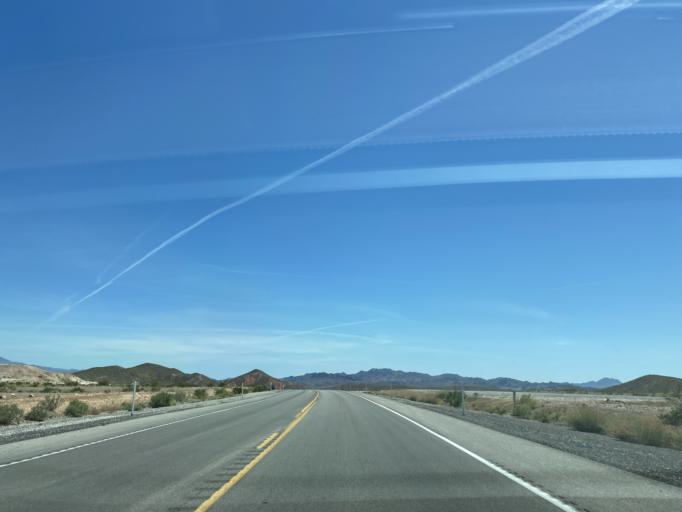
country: US
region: Nevada
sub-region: Clark County
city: Nellis Air Force Base
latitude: 36.1816
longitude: -114.9173
